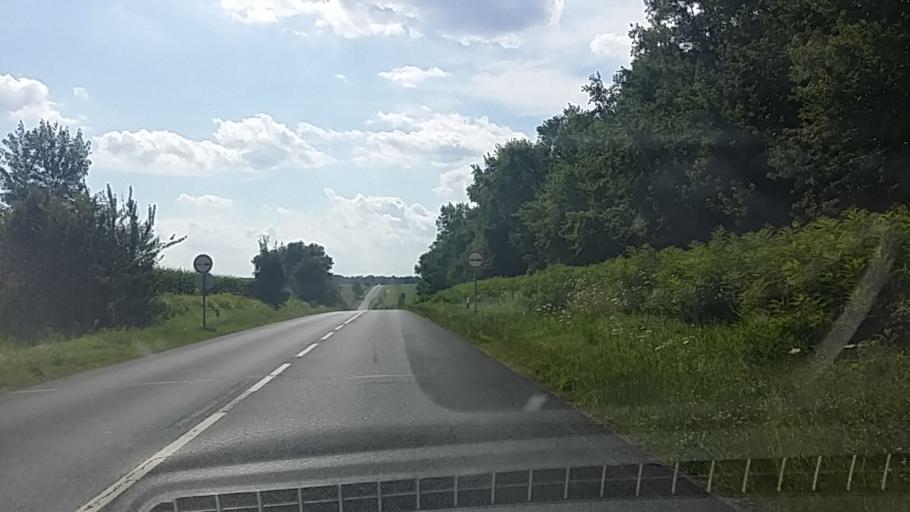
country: HU
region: Zala
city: Becsehely
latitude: 46.4581
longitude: 16.8683
